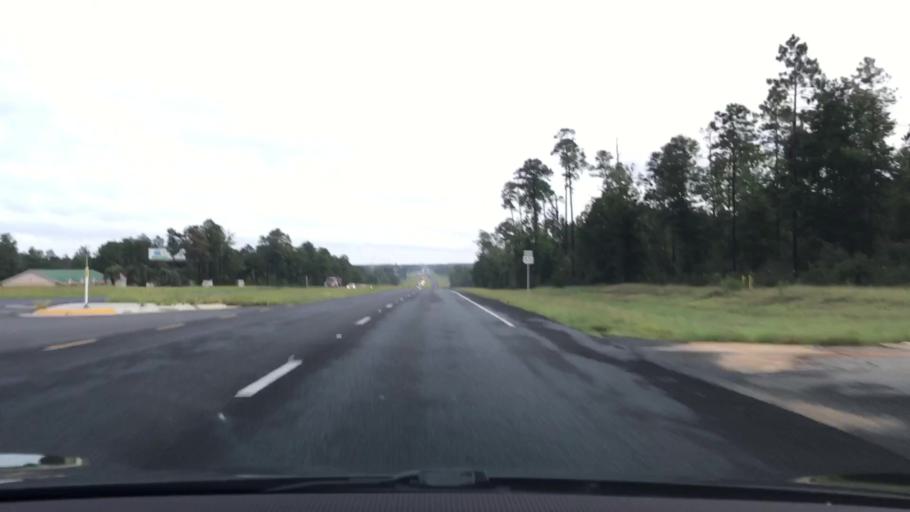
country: US
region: Florida
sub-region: Walton County
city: DeFuniak Springs
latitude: 30.6684
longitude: -86.1224
